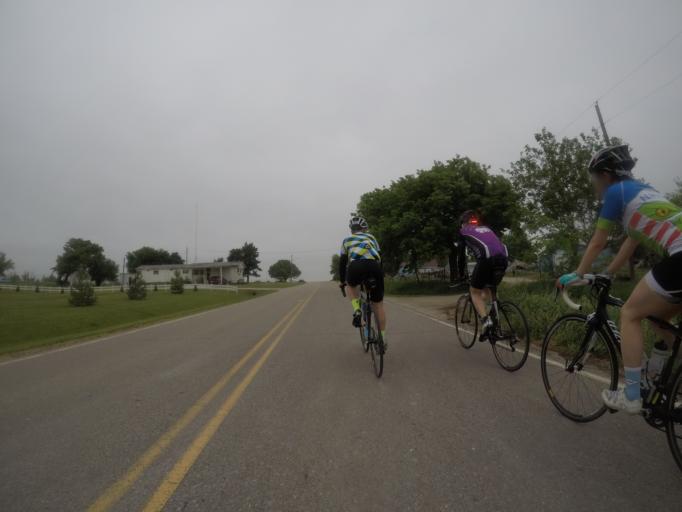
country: US
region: Kansas
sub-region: Pottawatomie County
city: Westmoreland
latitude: 39.5027
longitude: -96.3143
